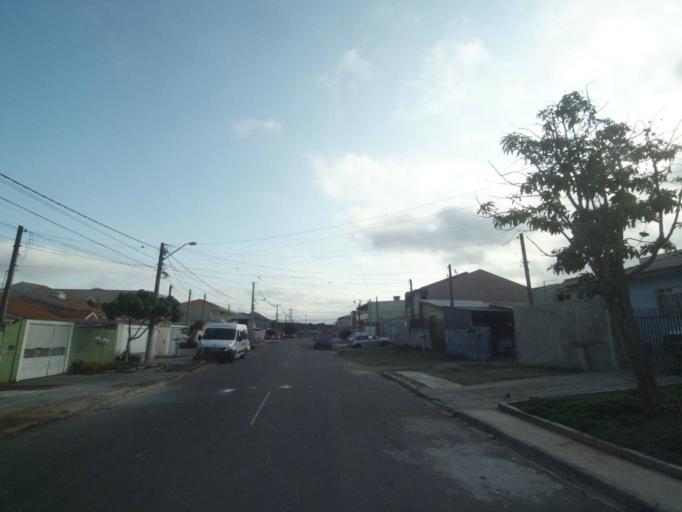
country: BR
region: Parana
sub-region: Sao Jose Dos Pinhais
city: Sao Jose dos Pinhais
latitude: -25.5479
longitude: -49.2544
